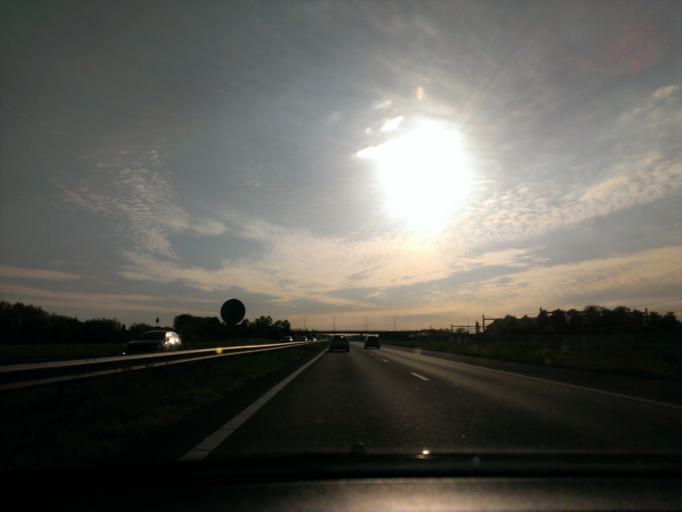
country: NL
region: Gelderland
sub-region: Gemeente Geldermalsen
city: Geldermalsen
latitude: 51.8589
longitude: 5.2871
